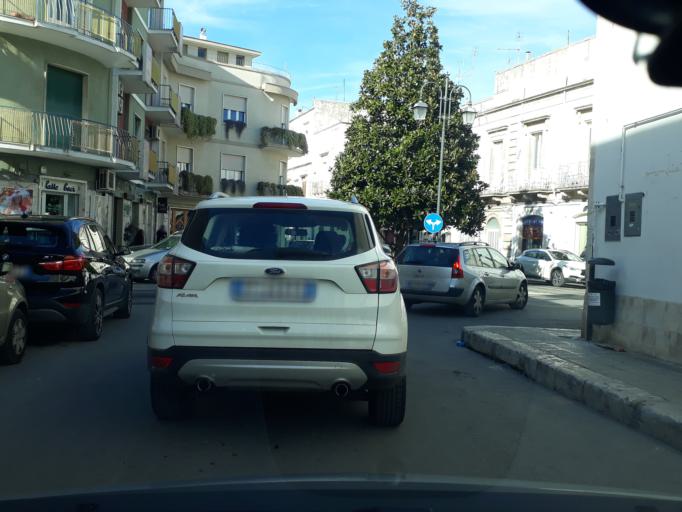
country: IT
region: Apulia
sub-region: Provincia di Taranto
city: Martina Franca
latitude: 40.7031
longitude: 17.3420
